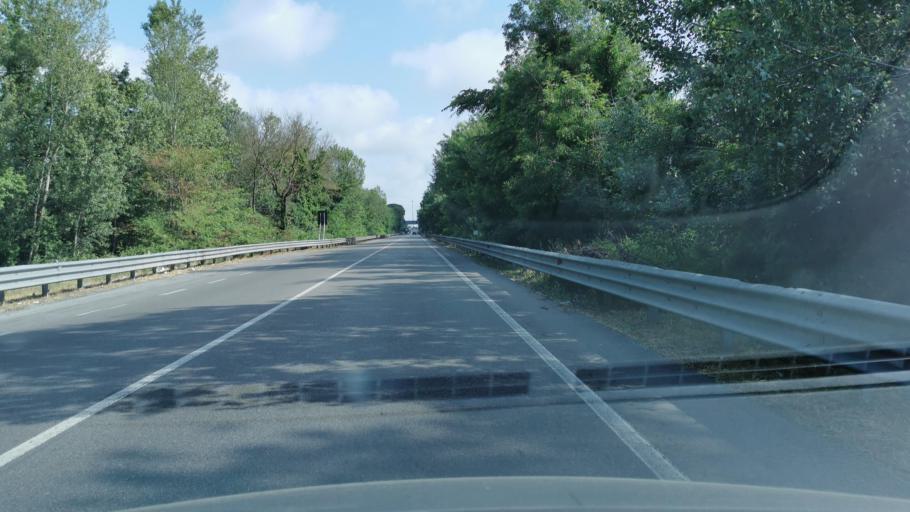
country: IT
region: Emilia-Romagna
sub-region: Provincia di Ravenna
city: Marina Romea
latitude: 44.5204
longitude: 12.2277
